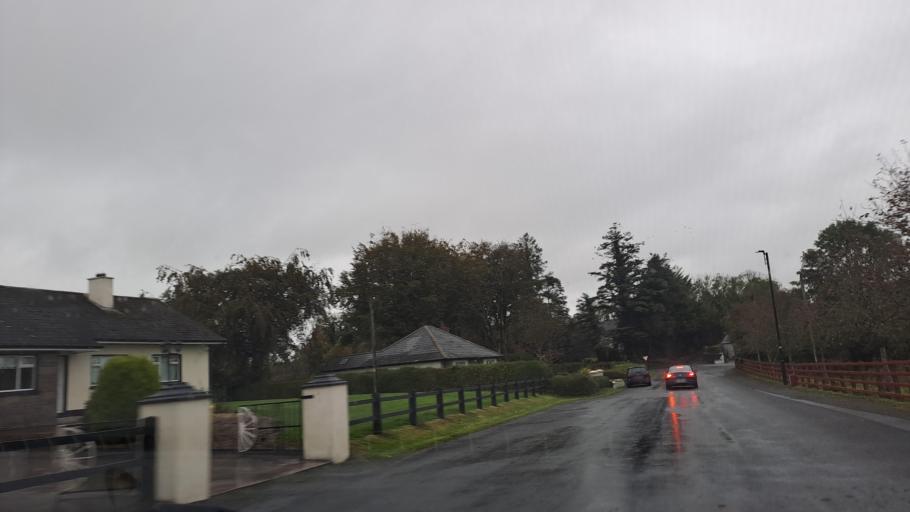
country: IE
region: Ulster
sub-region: County Monaghan
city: Monaghan
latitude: 54.2129
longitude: -6.9077
